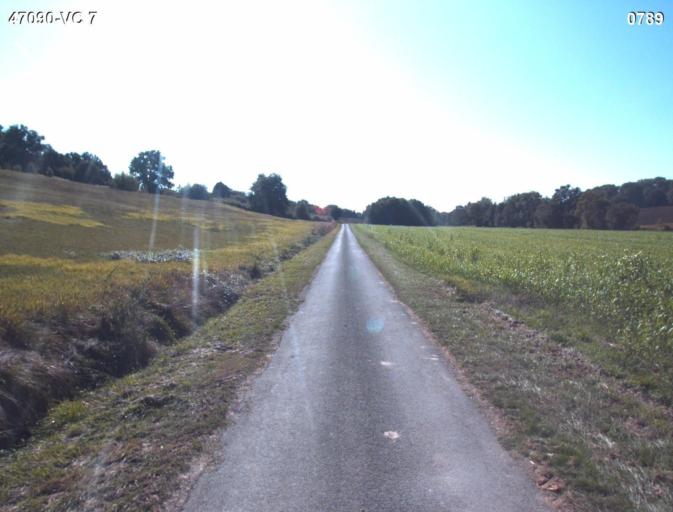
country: FR
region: Aquitaine
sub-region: Departement du Lot-et-Garonne
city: Nerac
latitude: 44.1736
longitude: 0.3639
